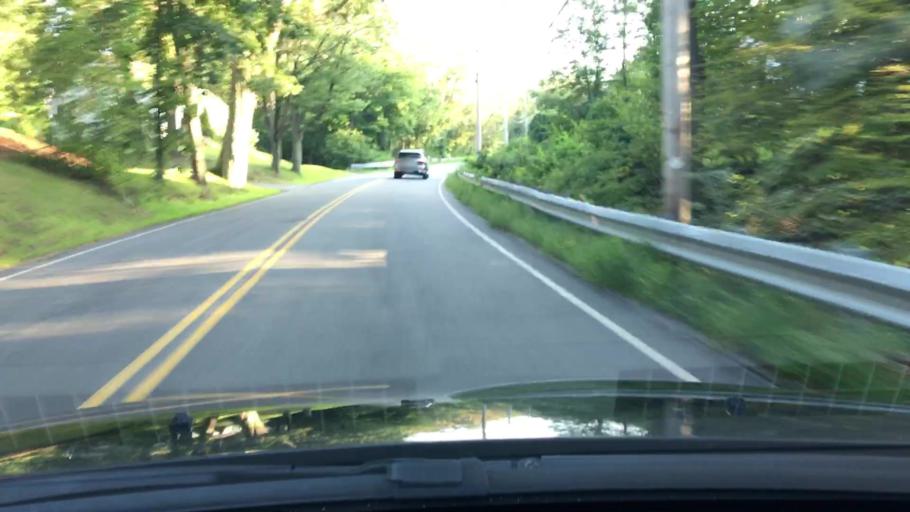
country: US
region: Massachusetts
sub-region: Worcester County
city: West Boylston
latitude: 42.3478
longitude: -71.7834
